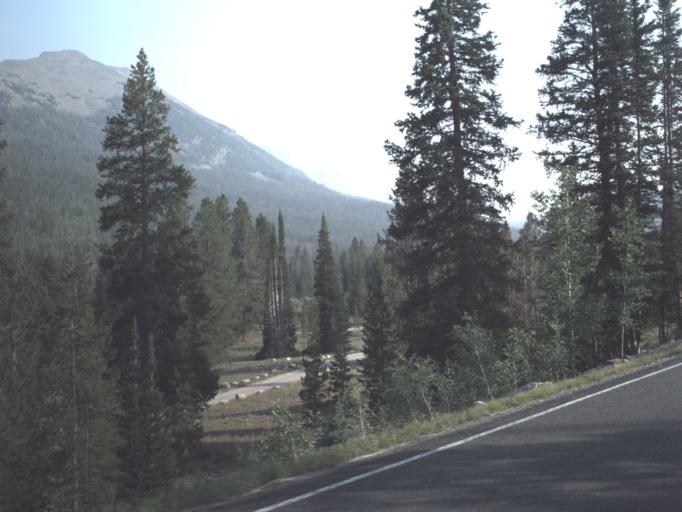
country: US
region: Utah
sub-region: Summit County
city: Kamas
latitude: 40.7903
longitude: -110.8852
